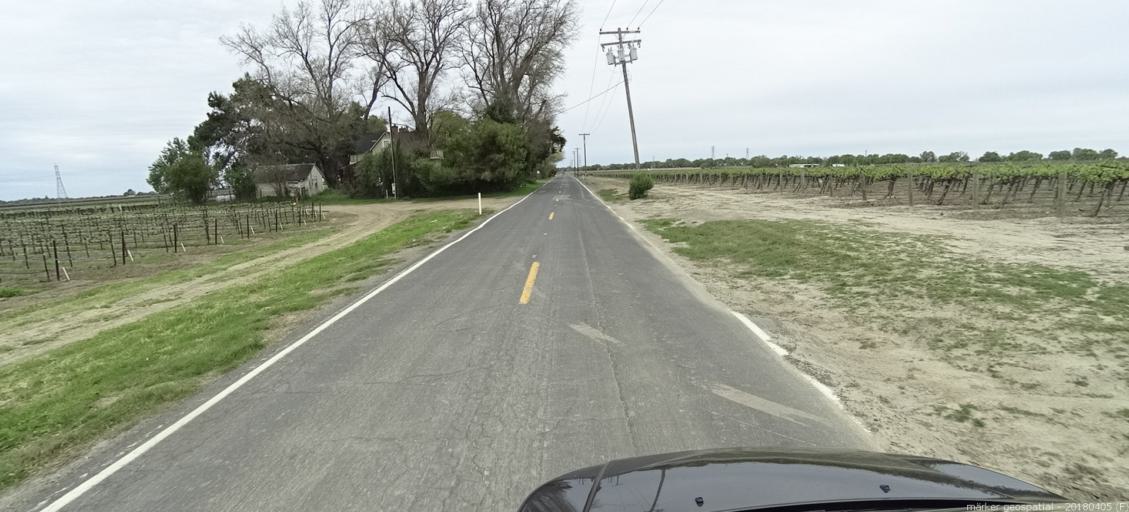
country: US
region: California
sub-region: Sacramento County
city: Walnut Grove
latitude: 38.3255
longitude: -121.5280
